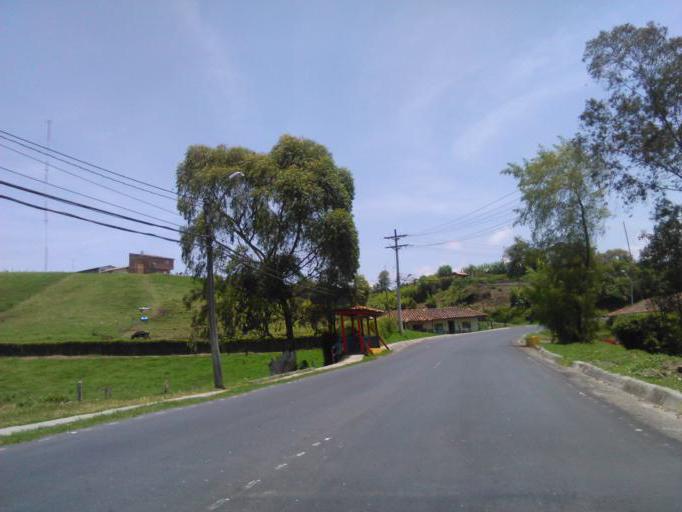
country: CO
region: Antioquia
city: La Union
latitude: 5.9801
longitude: -75.3697
